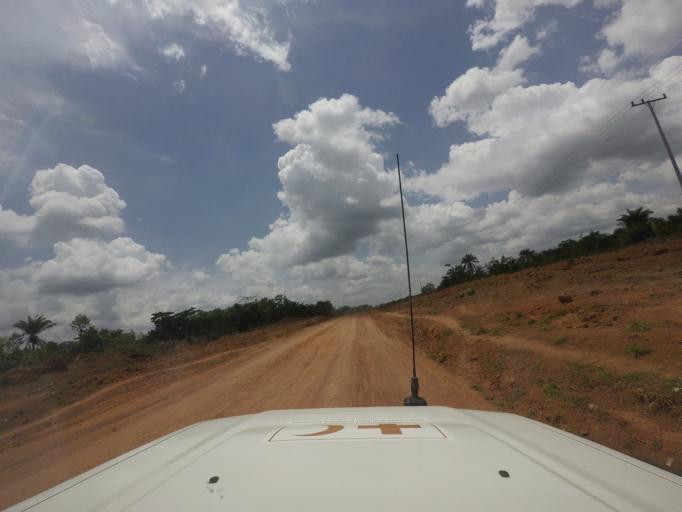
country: LR
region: Nimba
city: Sanniquellie
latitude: 7.2306
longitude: -8.8965
